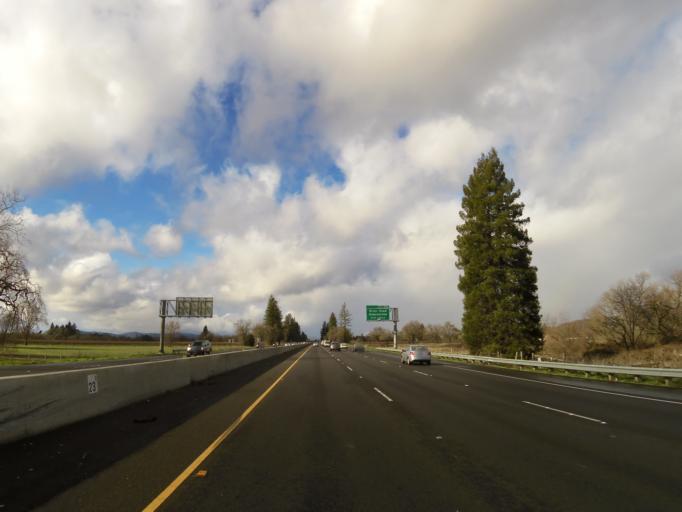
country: US
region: California
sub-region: Sonoma County
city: Larkfield-Wikiup
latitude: 38.4844
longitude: -122.7397
